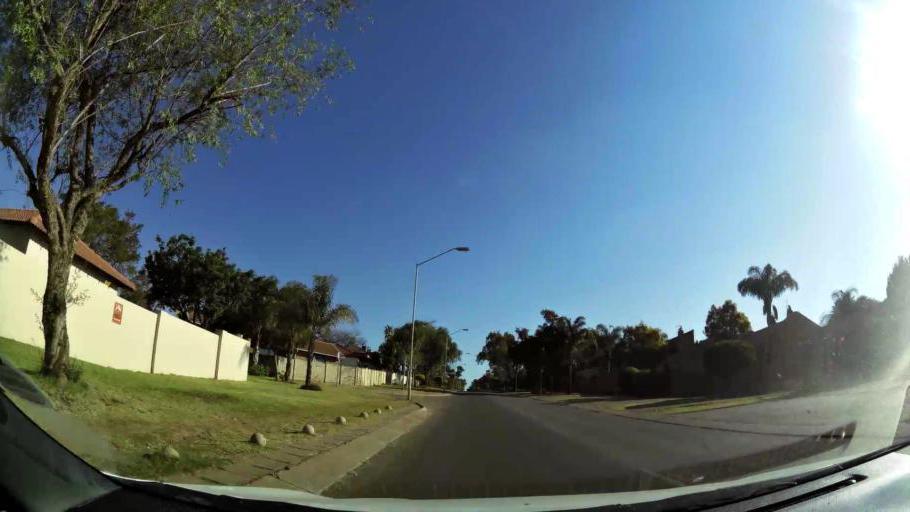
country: ZA
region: Gauteng
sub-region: City of Tshwane Metropolitan Municipality
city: Centurion
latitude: -25.8344
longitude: 28.2994
